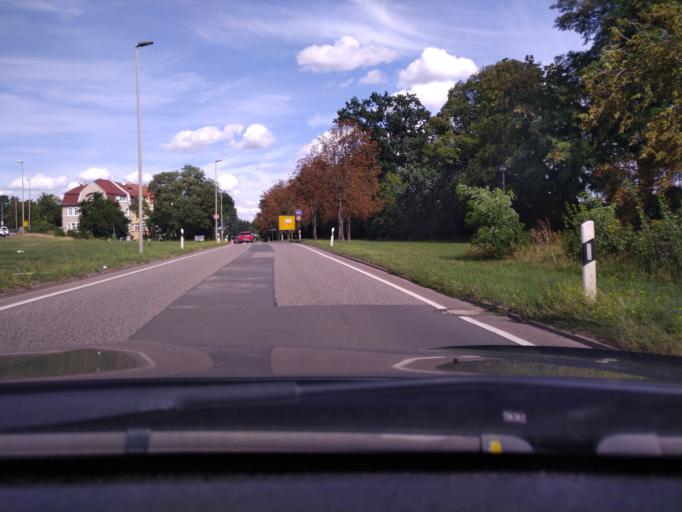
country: DE
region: Saxony-Anhalt
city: Magdeburg
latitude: 52.1379
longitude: 11.6283
